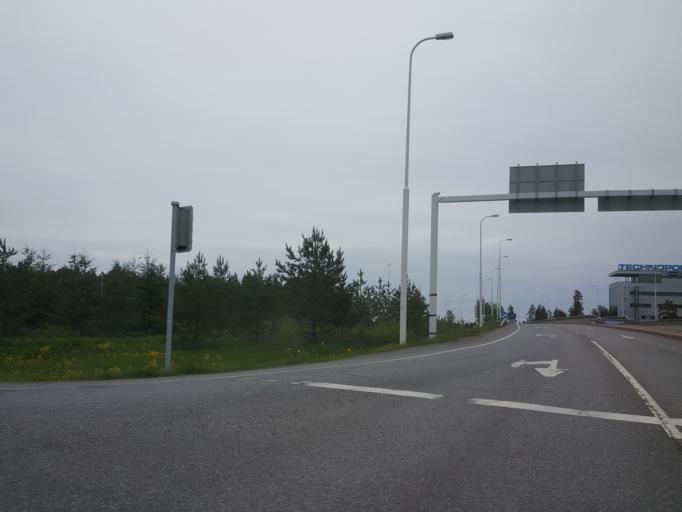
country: FI
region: Uusimaa
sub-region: Helsinki
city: Vantaa
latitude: 60.3076
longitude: 24.9635
